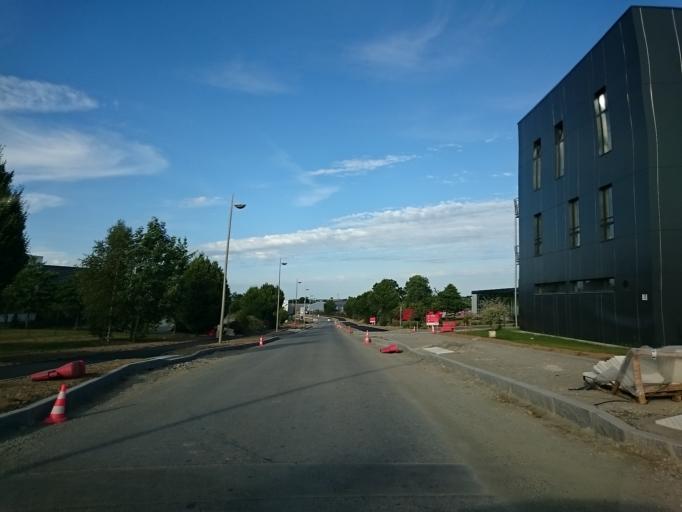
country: FR
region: Brittany
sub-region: Departement d'Ille-et-Vilaine
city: Bain-de-Bretagne
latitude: 47.8529
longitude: -1.6859
